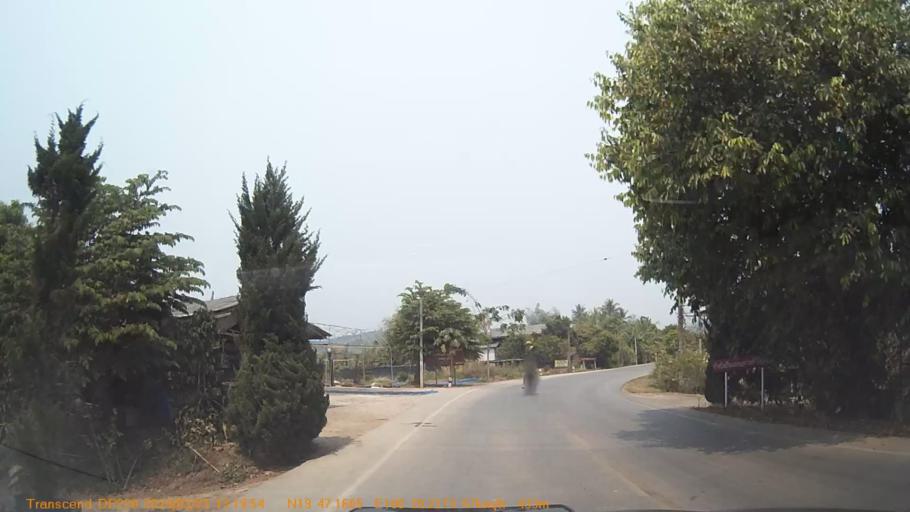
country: TH
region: Chiang Rai
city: Khun Tan
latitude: 19.7864
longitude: 100.3371
